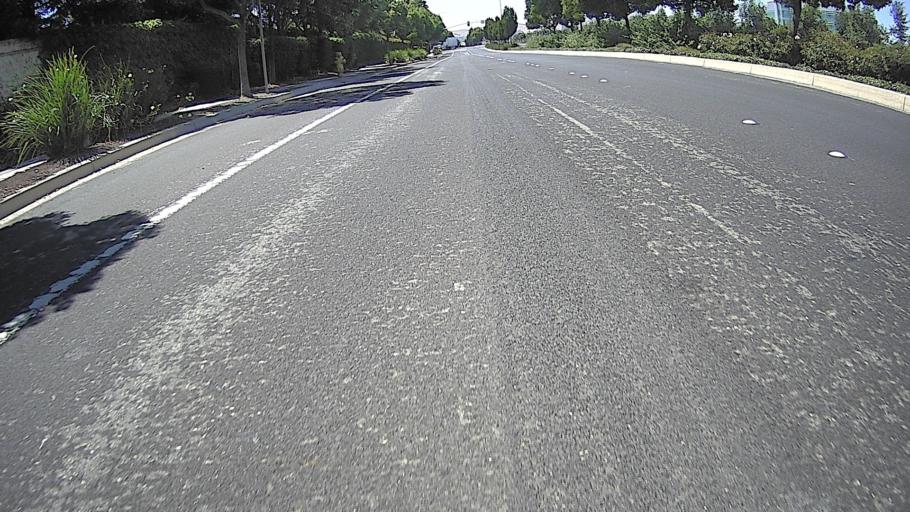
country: US
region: California
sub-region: Alameda County
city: Dublin
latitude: 37.7137
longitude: -121.8859
